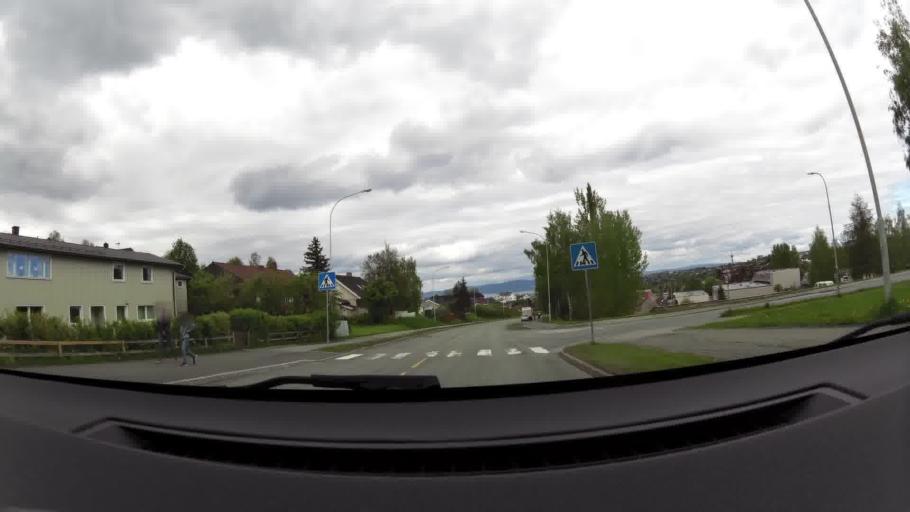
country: NO
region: Sor-Trondelag
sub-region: Trondheim
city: Trondheim
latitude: 63.3948
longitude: 10.4234
